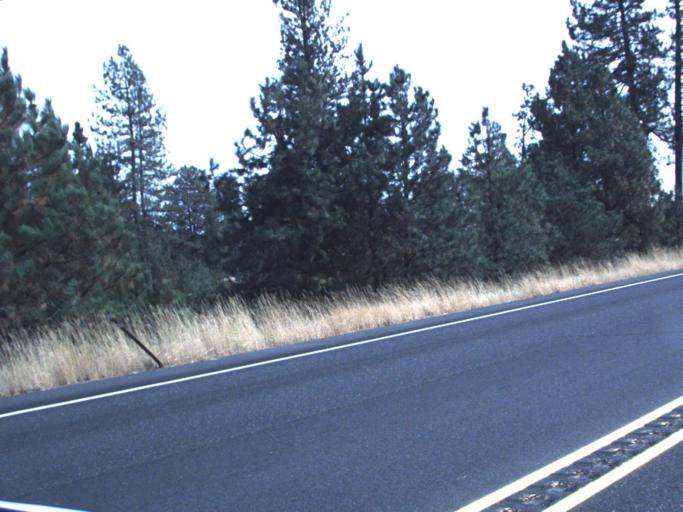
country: US
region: Washington
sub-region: Spokane County
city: Deer Park
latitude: 47.9082
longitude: -117.4441
